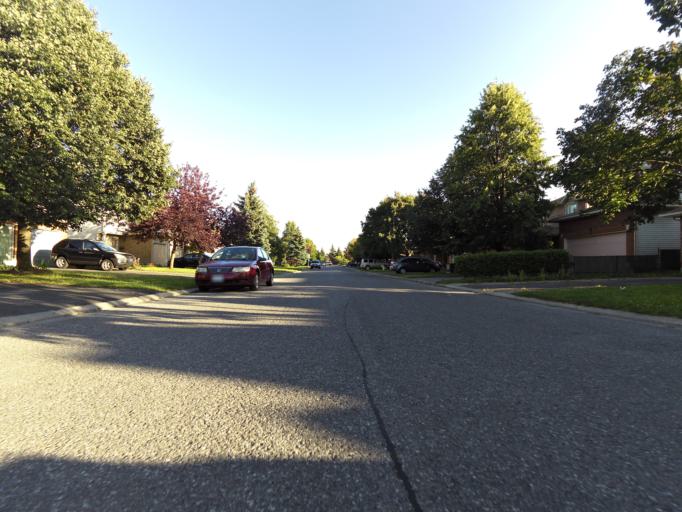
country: CA
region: Ontario
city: Bells Corners
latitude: 45.2862
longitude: -75.7253
